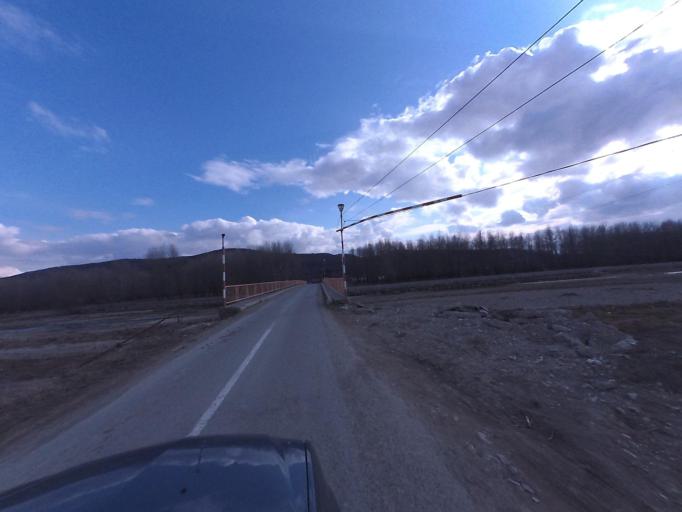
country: RO
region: Neamt
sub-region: Comuna Grumazesti
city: Topolita
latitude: 47.1998
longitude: 26.4063
